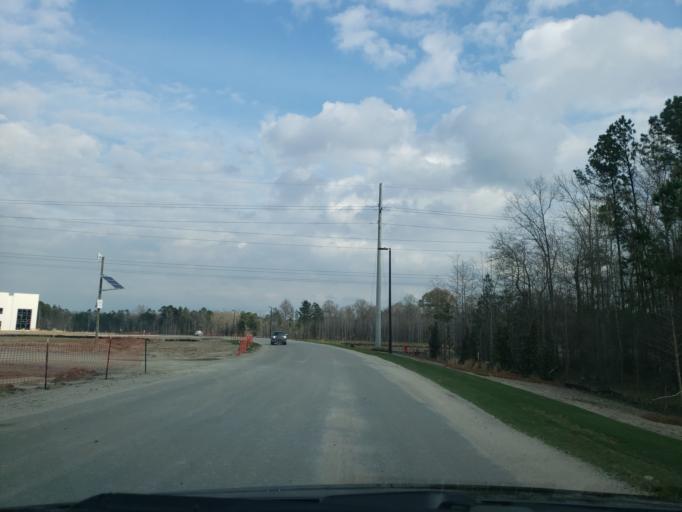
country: US
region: Georgia
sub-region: Effingham County
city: Rincon
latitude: 32.2356
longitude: -81.2041
